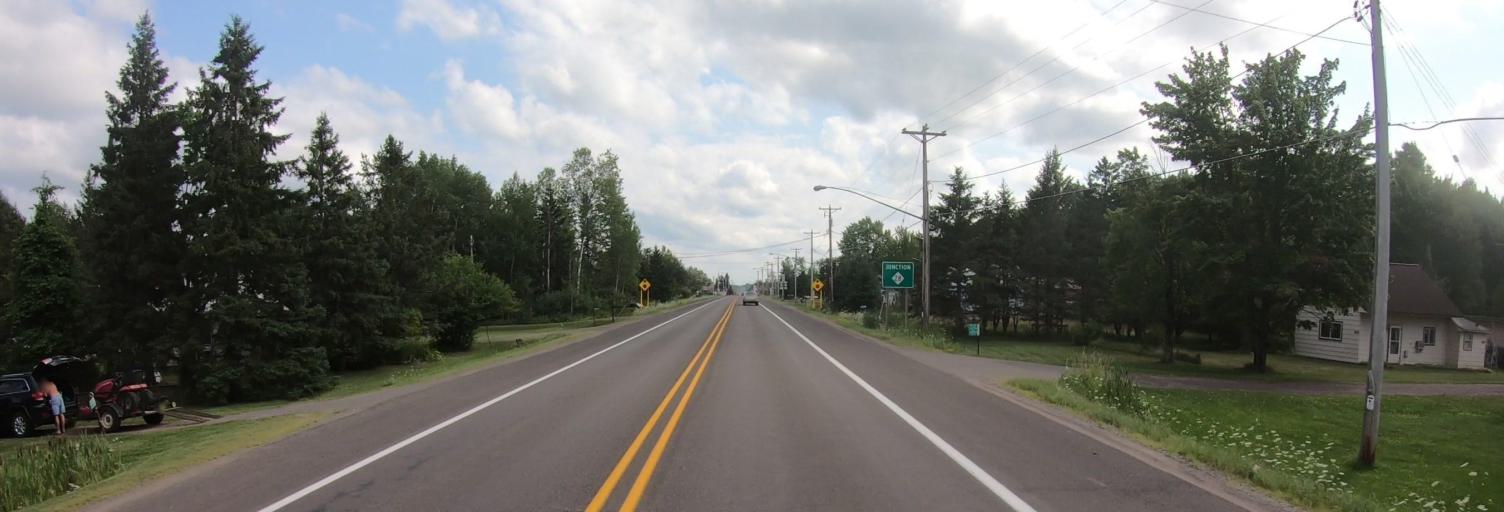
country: US
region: Michigan
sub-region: Ontonagon County
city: Ontonagon
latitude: 46.5389
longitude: -89.1786
